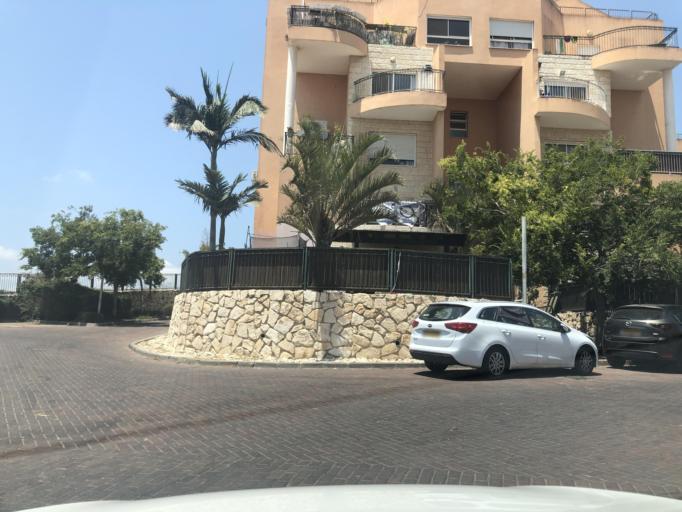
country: IL
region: Haifa
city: Daliyat el Karmil
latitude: 32.6348
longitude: 35.0936
